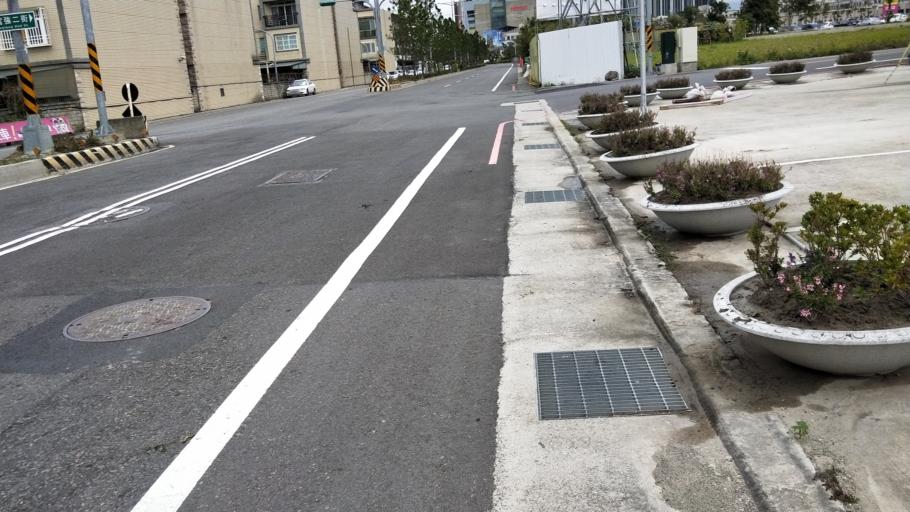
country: TW
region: Taiwan
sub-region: Hsinchu
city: Hsinchu
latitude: 24.6888
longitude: 120.8971
